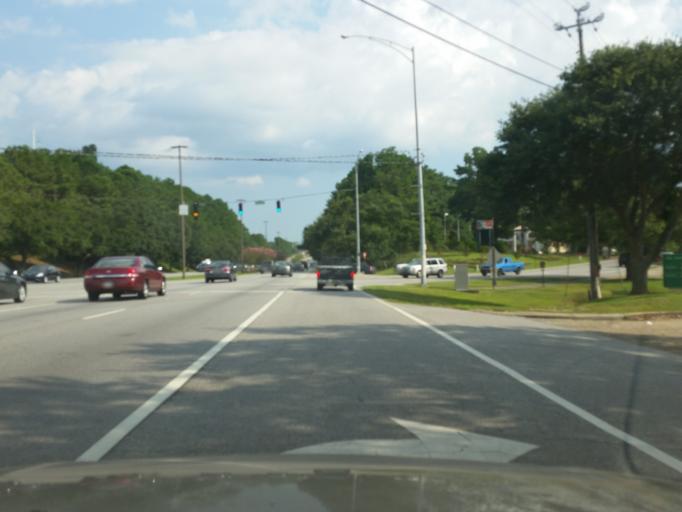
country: US
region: Alabama
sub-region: Baldwin County
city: Daphne
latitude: 30.6315
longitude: -87.9111
